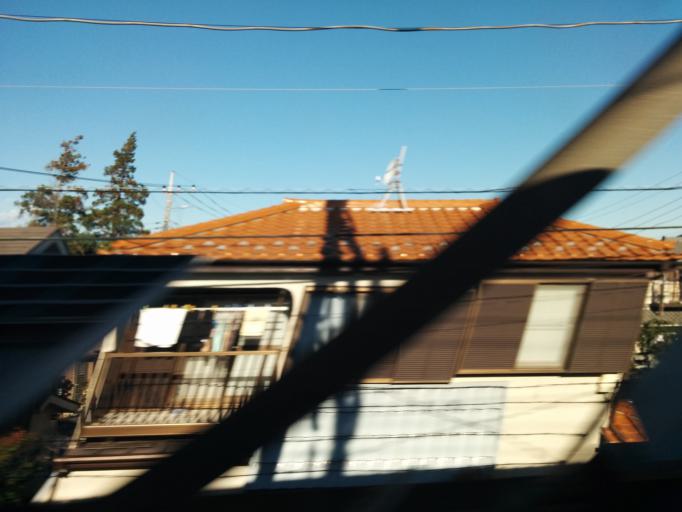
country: JP
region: Kanagawa
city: Yokohama
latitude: 35.4687
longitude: 139.5488
